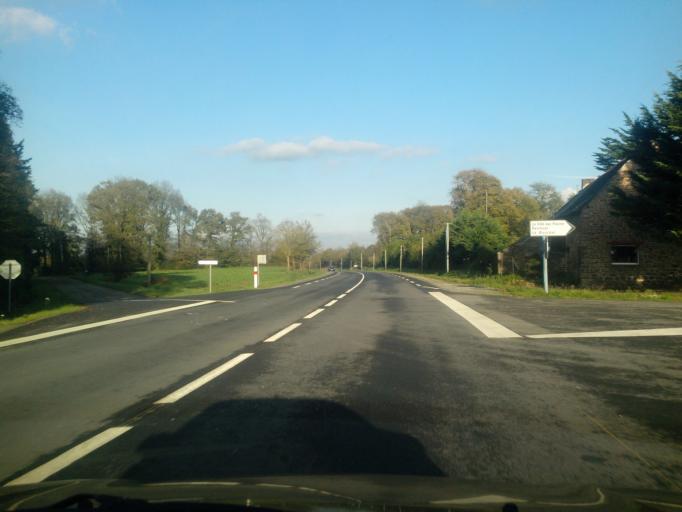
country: FR
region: Brittany
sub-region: Departement du Morbihan
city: Mauron
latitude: 48.0302
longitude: -2.3072
